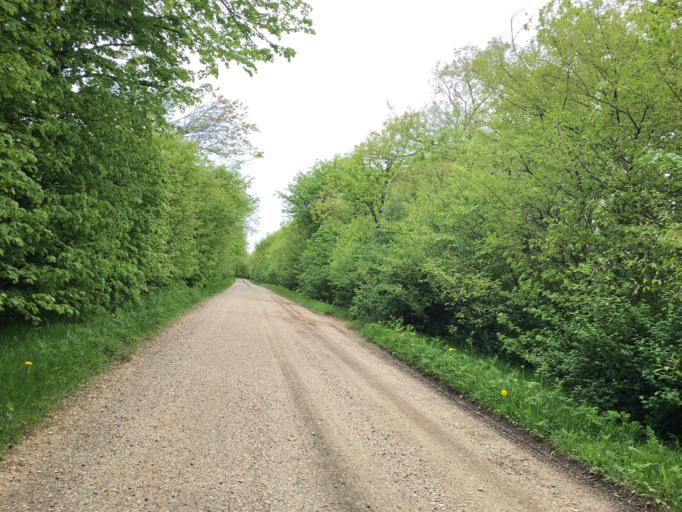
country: DK
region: Central Jutland
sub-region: Holstebro Kommune
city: Ulfborg
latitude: 56.2663
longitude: 8.4254
